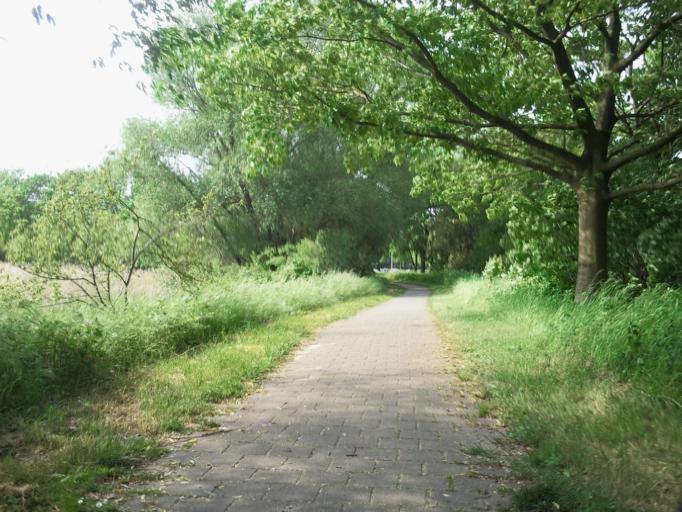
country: DE
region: Lower Saxony
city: Nienburg
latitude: 52.6308
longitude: 9.2089
